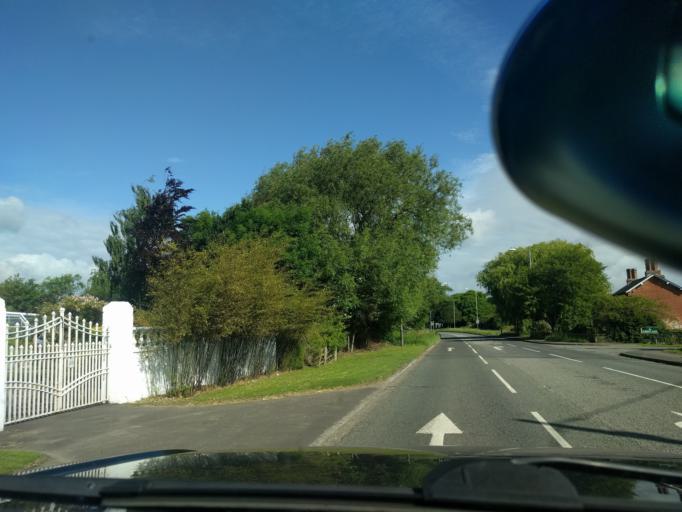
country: GB
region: England
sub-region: Wiltshire
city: Bremhill
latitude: 51.4422
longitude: -2.0770
